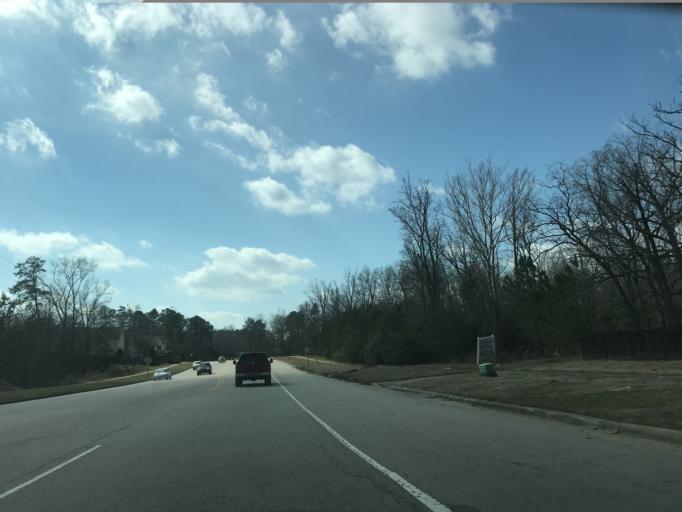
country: US
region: North Carolina
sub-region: Durham County
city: Gorman
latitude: 35.9755
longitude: -78.7941
